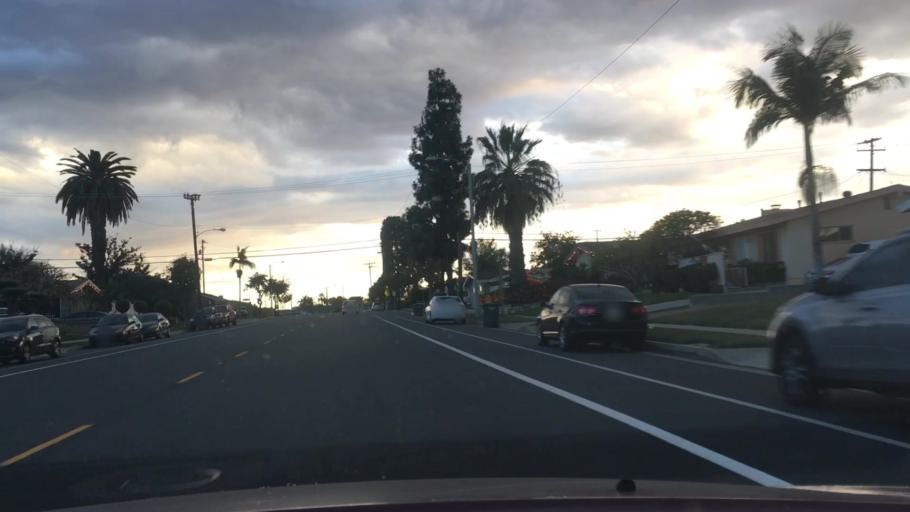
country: US
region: California
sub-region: Los Angeles County
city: La Mirada
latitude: 33.9131
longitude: -118.0204
